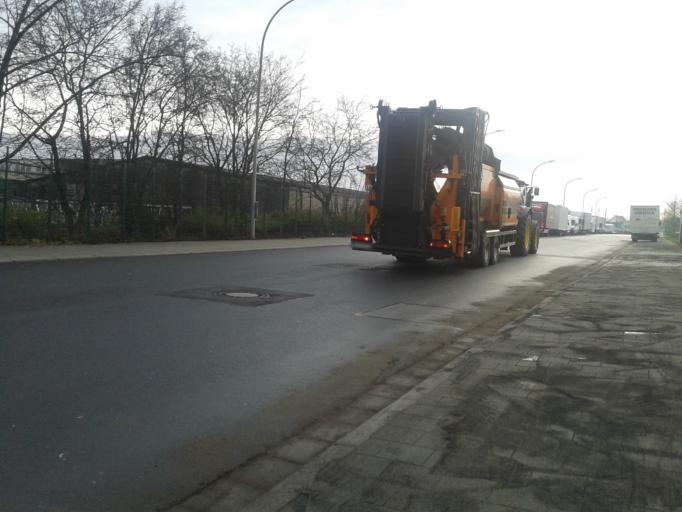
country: DE
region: Bavaria
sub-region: Upper Franconia
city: Hallstadt
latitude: 49.9113
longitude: 10.8778
